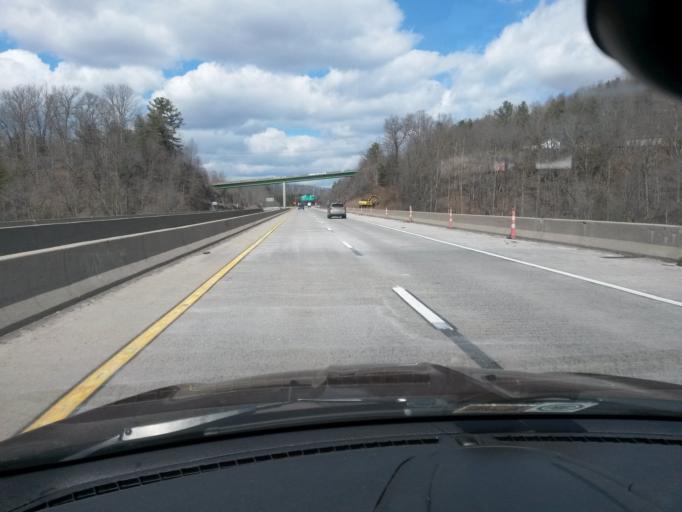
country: US
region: West Virginia
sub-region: Raleigh County
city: Beaver
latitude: 37.7551
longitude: -81.1510
